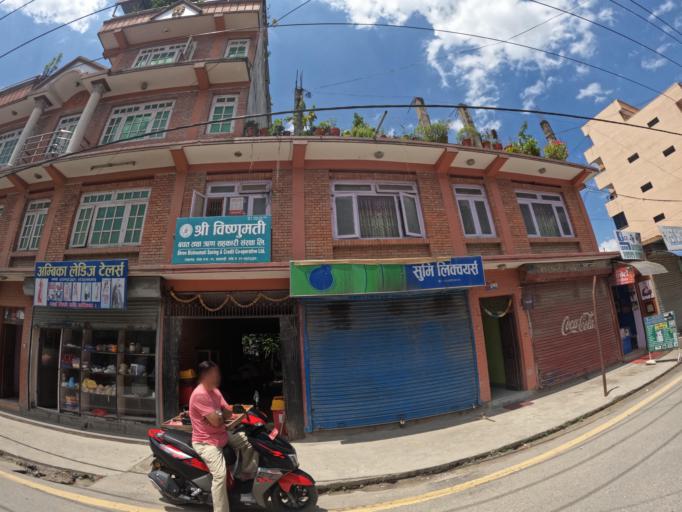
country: NP
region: Central Region
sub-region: Bagmati Zone
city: Kathmandu
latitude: 27.7430
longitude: 85.3223
